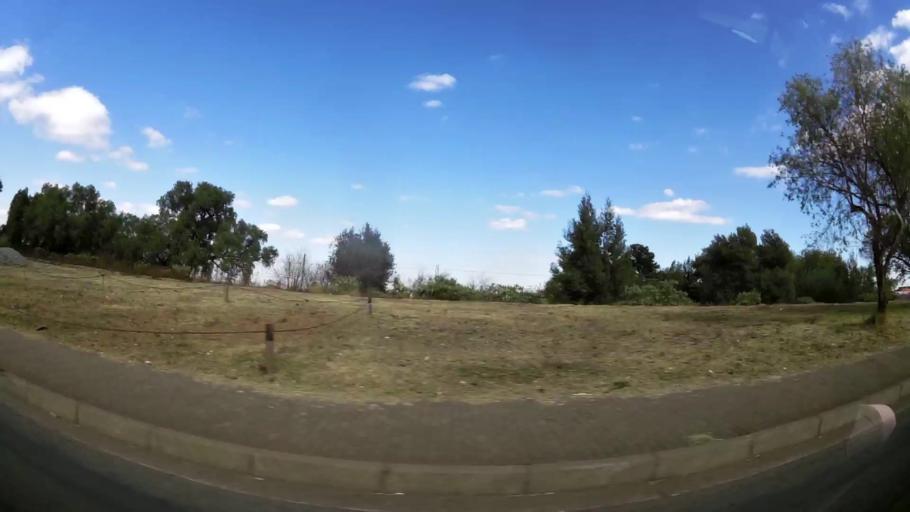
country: ZA
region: Gauteng
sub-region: West Rand District Municipality
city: Krugersdorp
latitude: -26.1198
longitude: 27.8155
